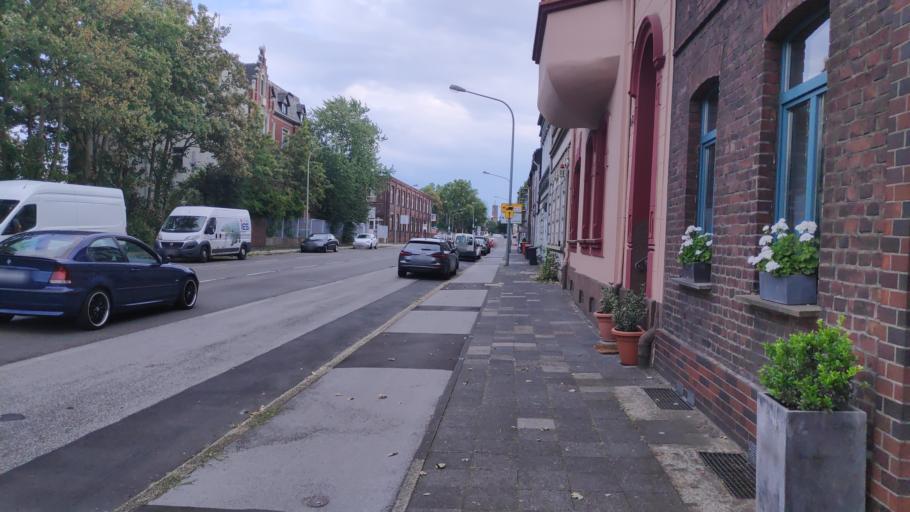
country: DE
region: North Rhine-Westphalia
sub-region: Regierungsbezirk Dusseldorf
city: Krefeld
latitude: 51.3645
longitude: 6.6481
